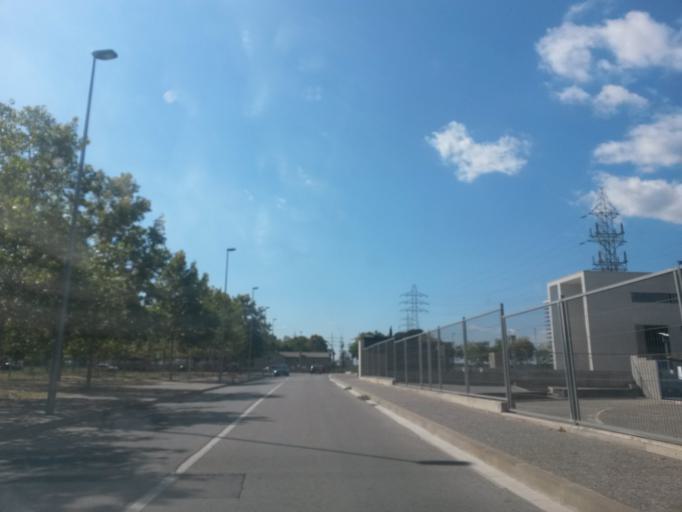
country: ES
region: Catalonia
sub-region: Provincia de Girona
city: Salt
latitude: 41.9692
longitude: 2.8021
